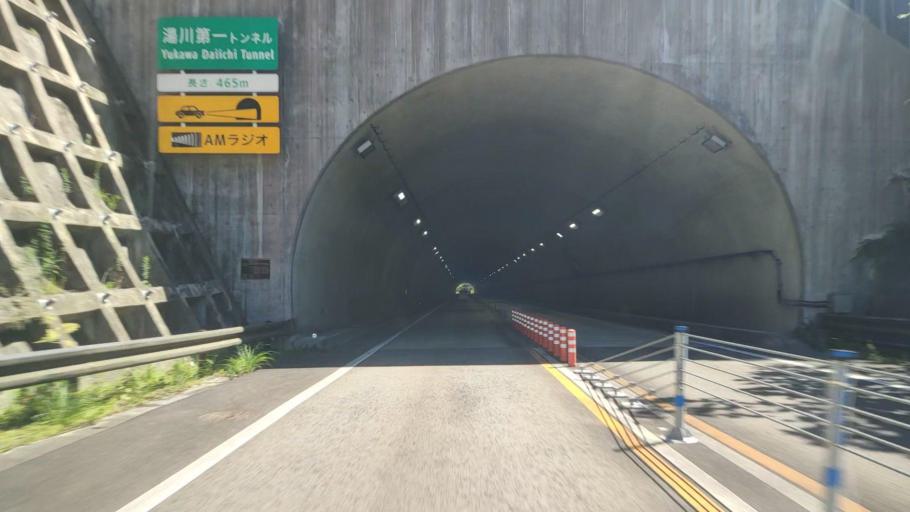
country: JP
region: Wakayama
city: Shingu
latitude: 33.6256
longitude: 135.9207
